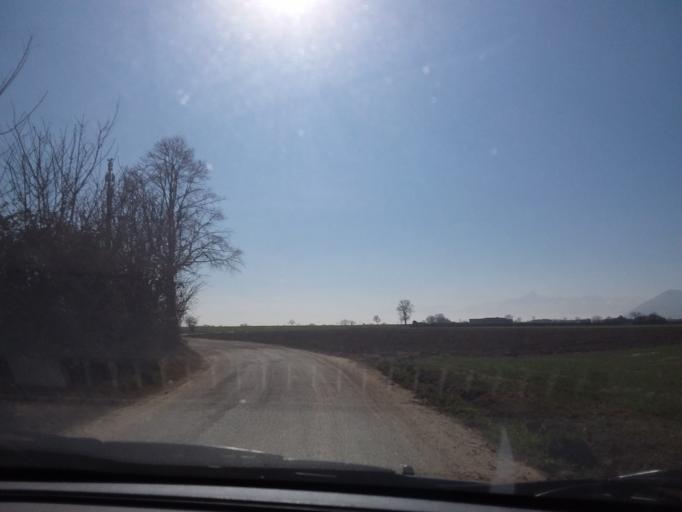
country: IT
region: Piedmont
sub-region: Provincia di Torino
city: Tetti Neirotti
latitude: 45.0498
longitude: 7.5412
